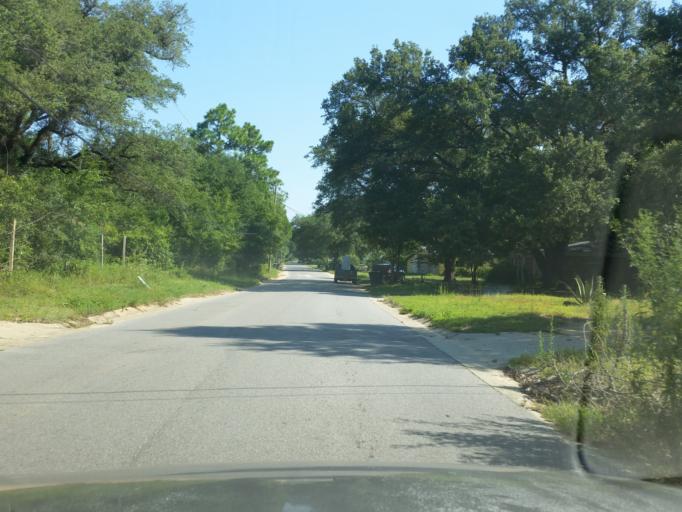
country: US
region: Florida
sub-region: Escambia County
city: Ferry Pass
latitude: 30.5118
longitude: -87.2044
